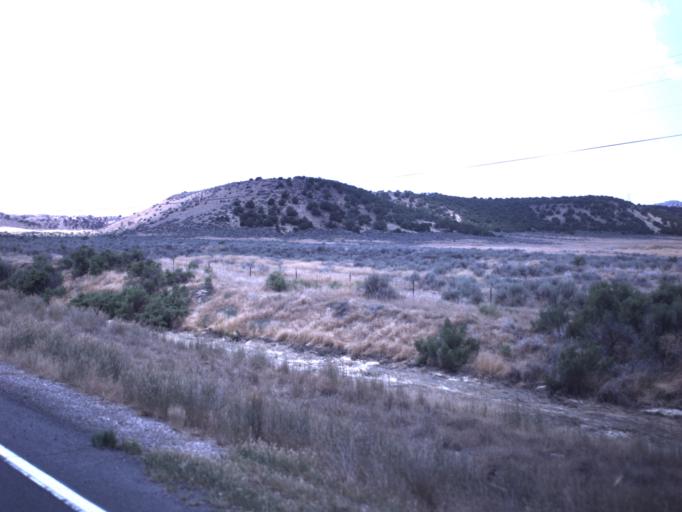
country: US
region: Utah
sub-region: Uintah County
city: Maeser
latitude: 40.4600
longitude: -109.6146
